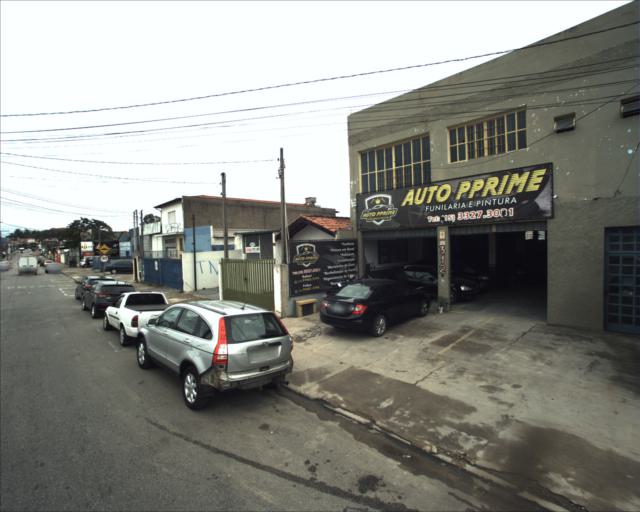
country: BR
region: Sao Paulo
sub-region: Sorocaba
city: Sorocaba
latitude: -23.5147
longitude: -47.4404
